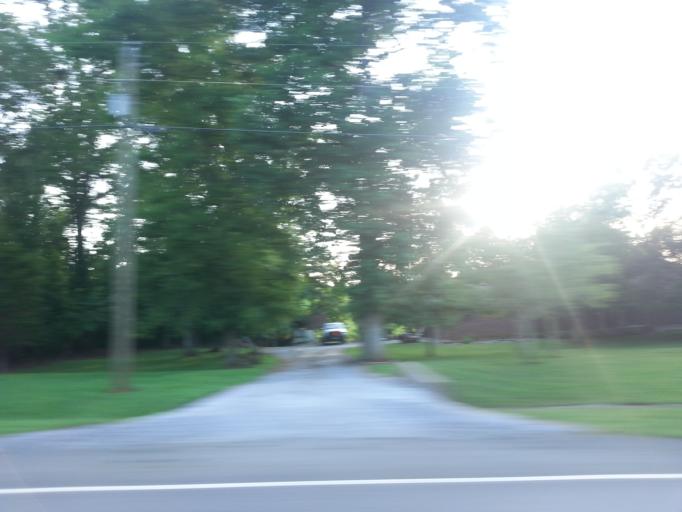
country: US
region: Tennessee
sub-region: Loudon County
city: Greenback
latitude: 35.6868
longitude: -84.2305
